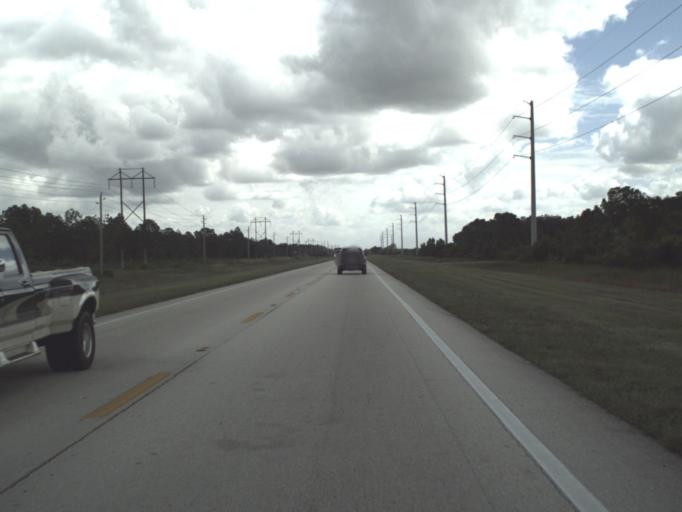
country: US
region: Florida
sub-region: Lee County
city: Gateway
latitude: 26.5707
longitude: -81.6883
